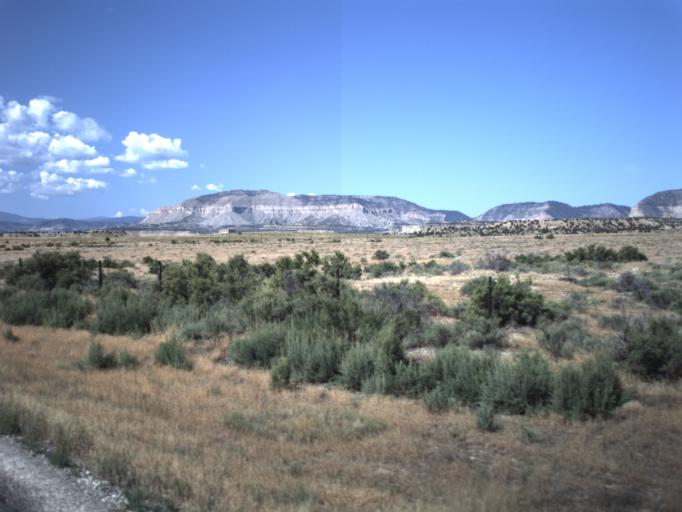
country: US
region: Utah
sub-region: Emery County
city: Ferron
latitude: 38.9177
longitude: -111.2631
